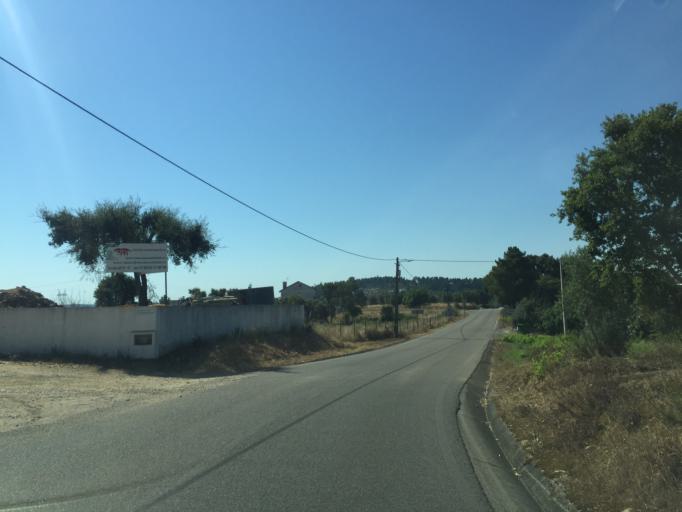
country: PT
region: Santarem
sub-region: Tomar
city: Tomar
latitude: 39.5800
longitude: -8.3258
